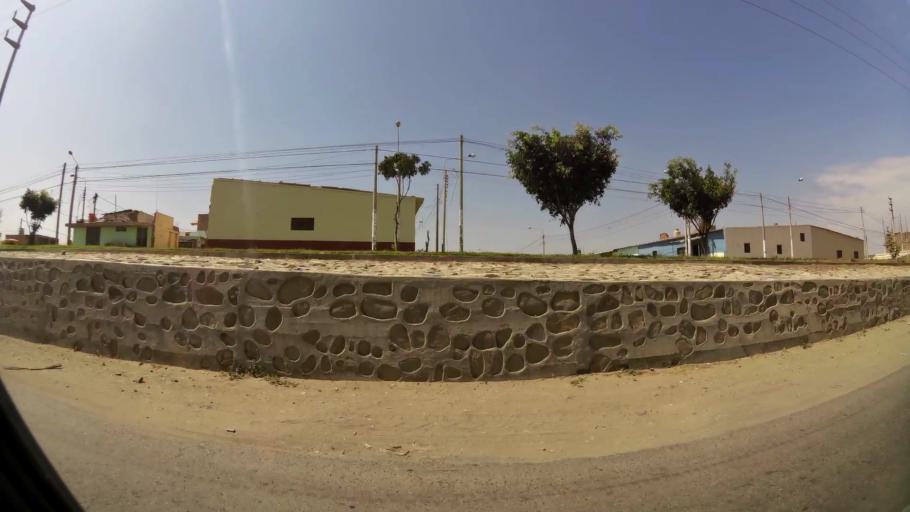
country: PE
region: Lambayeque
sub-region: Provincia de Chiclayo
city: Mocupe
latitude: -6.9864
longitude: -79.6284
